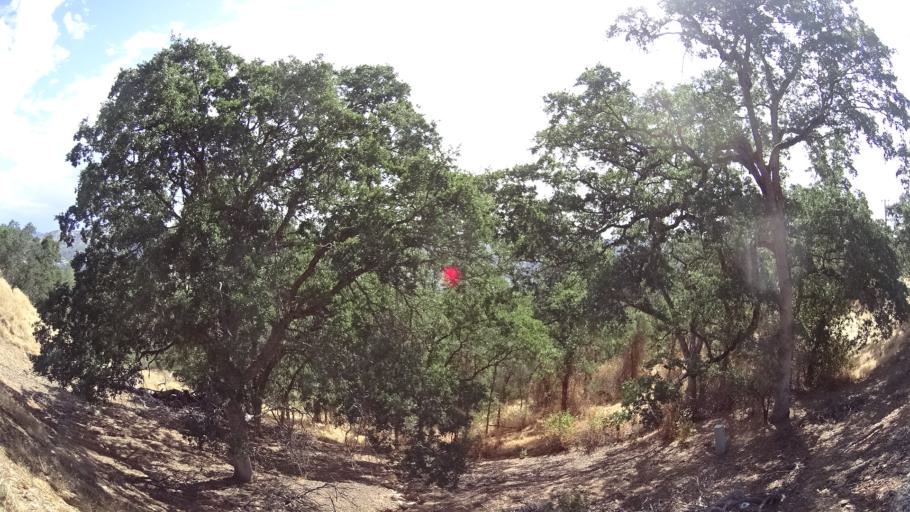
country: US
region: California
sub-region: Calaveras County
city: Copperopolis
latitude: 37.9140
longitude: -120.6128
